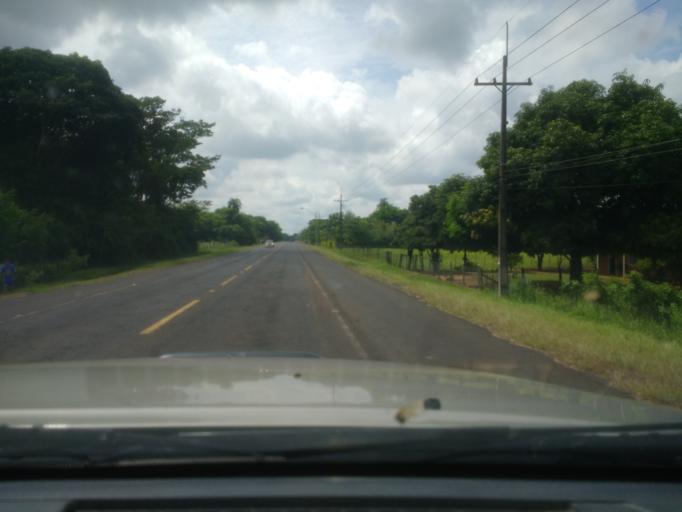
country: PY
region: San Pedro
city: Puerto Rosario
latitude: -24.4205
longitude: -57.0918
